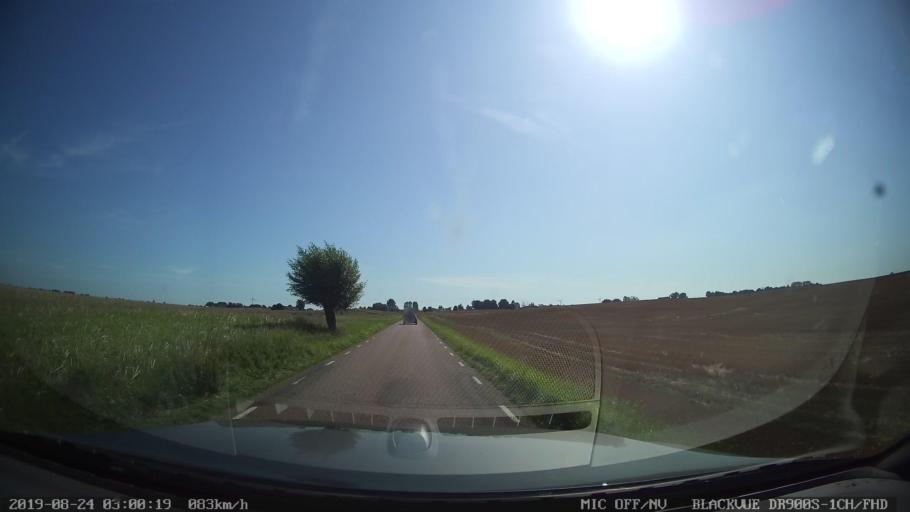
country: SE
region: Skane
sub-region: Skurups Kommun
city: Skurup
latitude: 55.4580
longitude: 13.4290
